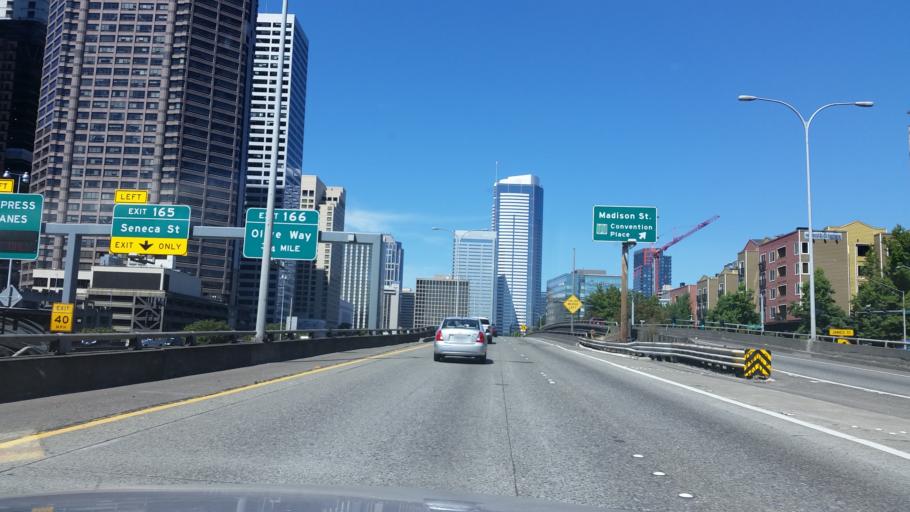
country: US
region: Washington
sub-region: King County
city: Seattle
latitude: 47.6038
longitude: -122.3267
